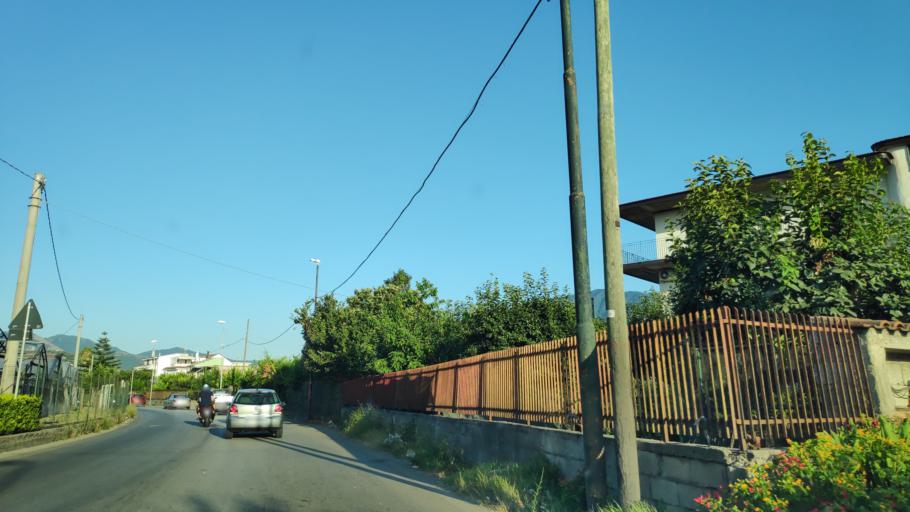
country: IT
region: Campania
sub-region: Provincia di Salerno
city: Pagani
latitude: 40.7631
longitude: 14.6127
